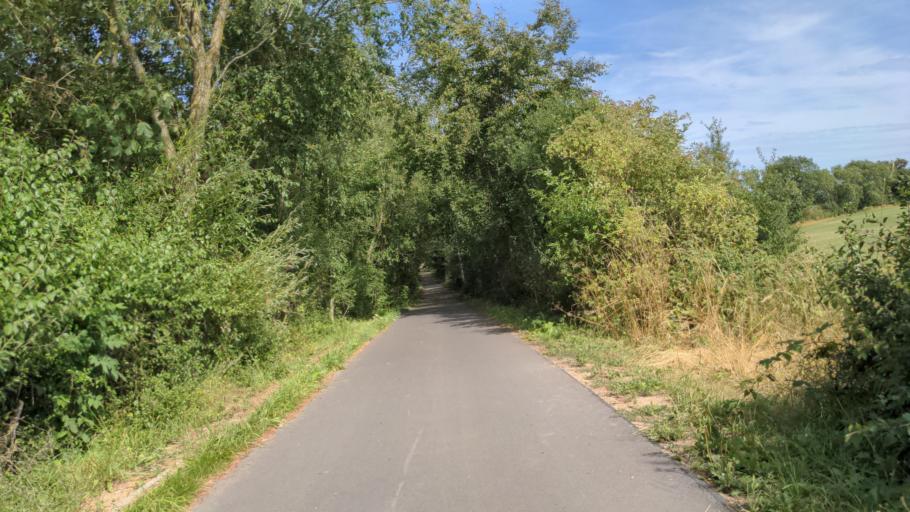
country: DE
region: Mecklenburg-Vorpommern
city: Klutz
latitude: 54.0090
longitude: 11.1396
